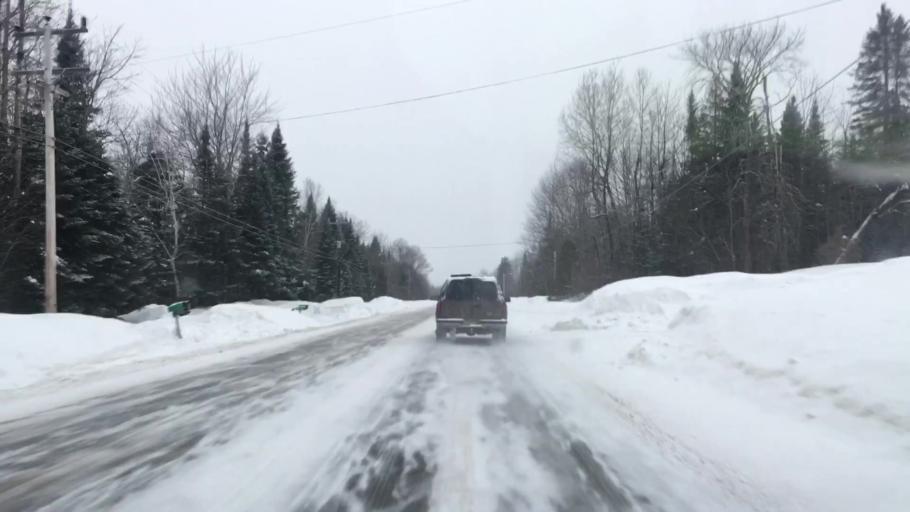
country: US
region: Maine
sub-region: Penobscot County
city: Medway
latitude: 45.5872
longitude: -68.4361
